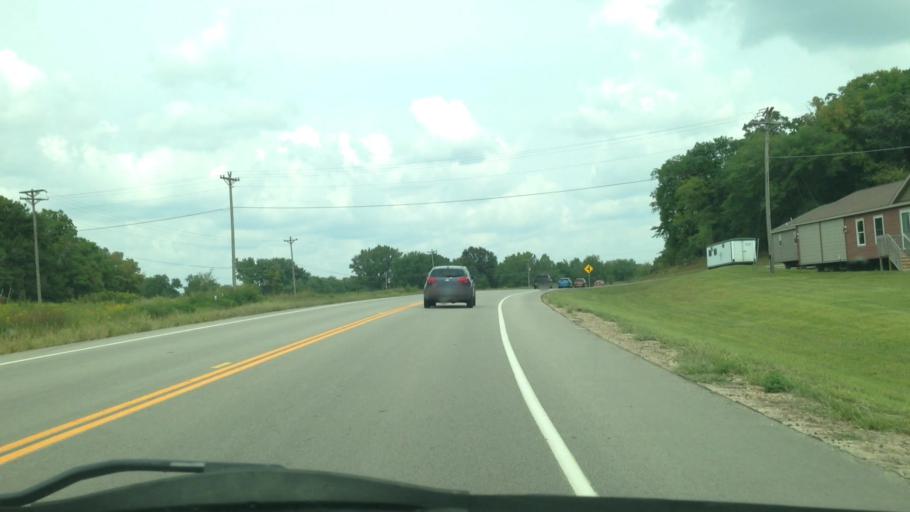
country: US
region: Minnesota
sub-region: Olmsted County
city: Rochester
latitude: 44.0767
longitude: -92.4502
